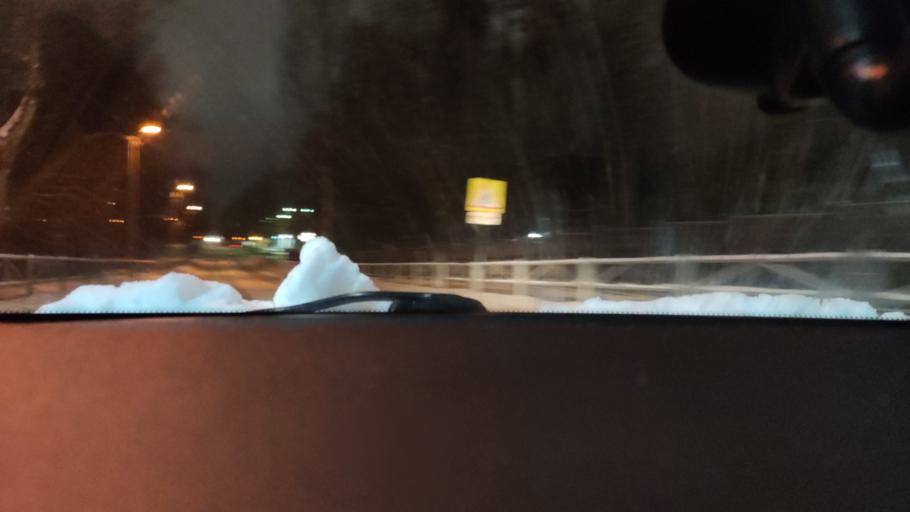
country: RU
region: Perm
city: Krasnokamsk
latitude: 58.0839
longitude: 55.7458
